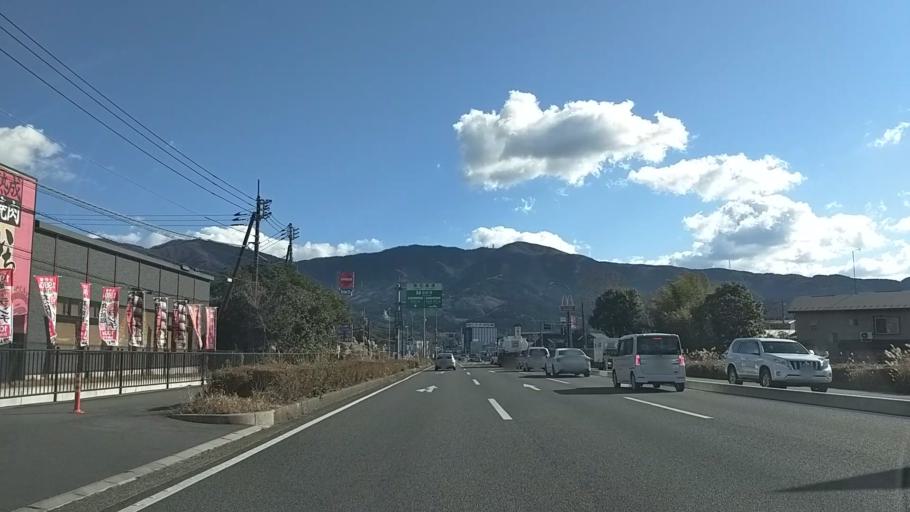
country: JP
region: Shizuoka
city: Gotemba
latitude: 35.3018
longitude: 138.9454
